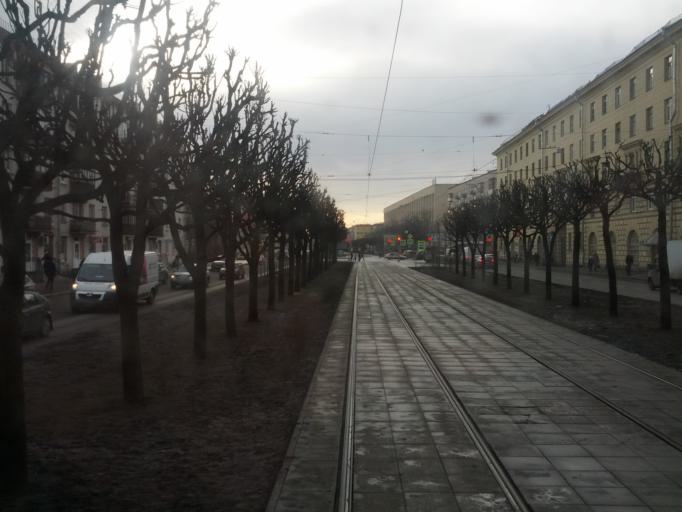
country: RU
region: St.-Petersburg
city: Centralniy
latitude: 59.9258
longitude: 30.4150
